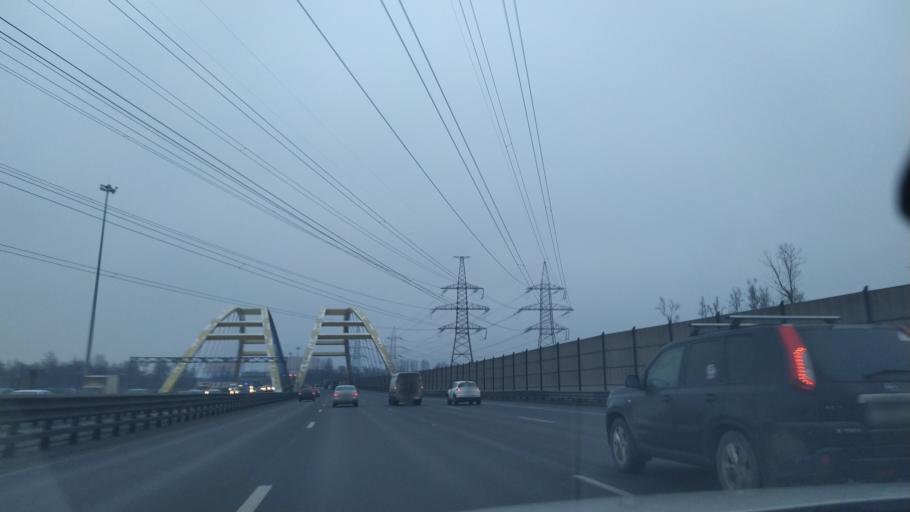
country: RU
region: St.-Petersburg
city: Krasnogvargeisky
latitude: 59.9866
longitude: 30.4897
